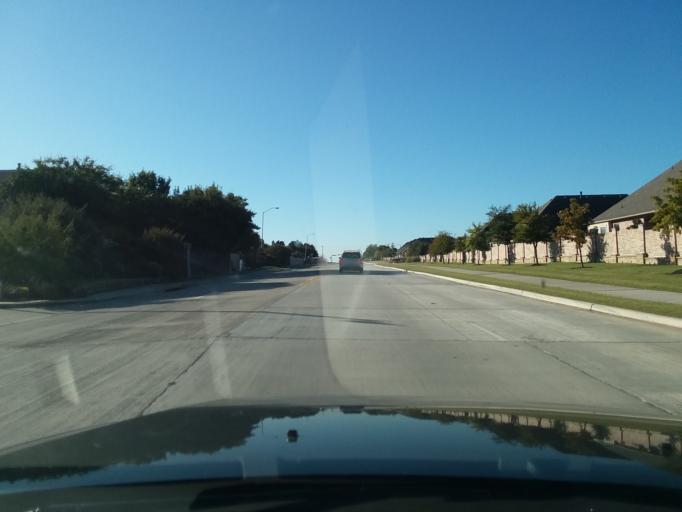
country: US
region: Texas
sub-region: Denton County
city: Lewisville
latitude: 33.0135
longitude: -97.0277
